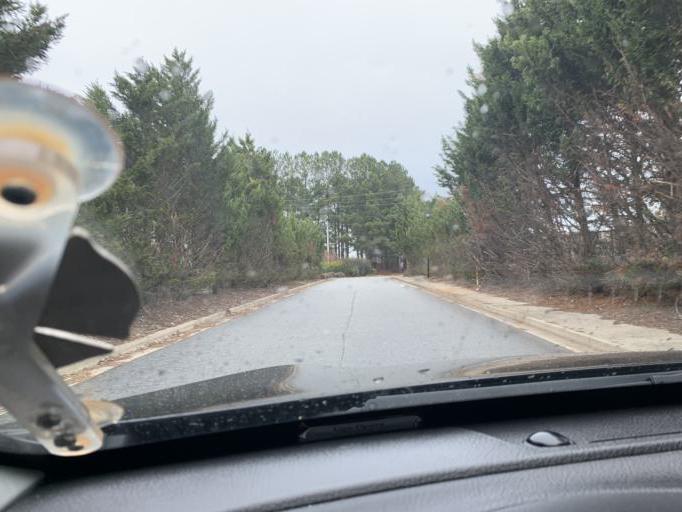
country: US
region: Georgia
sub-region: Cobb County
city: Acworth
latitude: 34.0732
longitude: -84.6509
